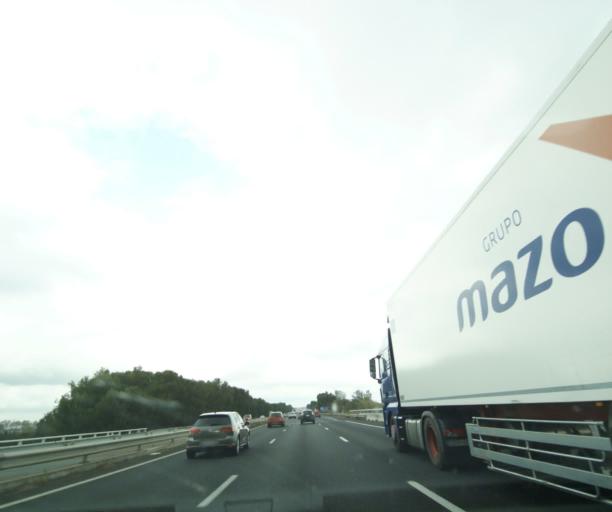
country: FR
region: Languedoc-Roussillon
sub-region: Departement de l'Herault
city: Villeneuve-les-Beziers
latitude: 43.3178
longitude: 3.2621
